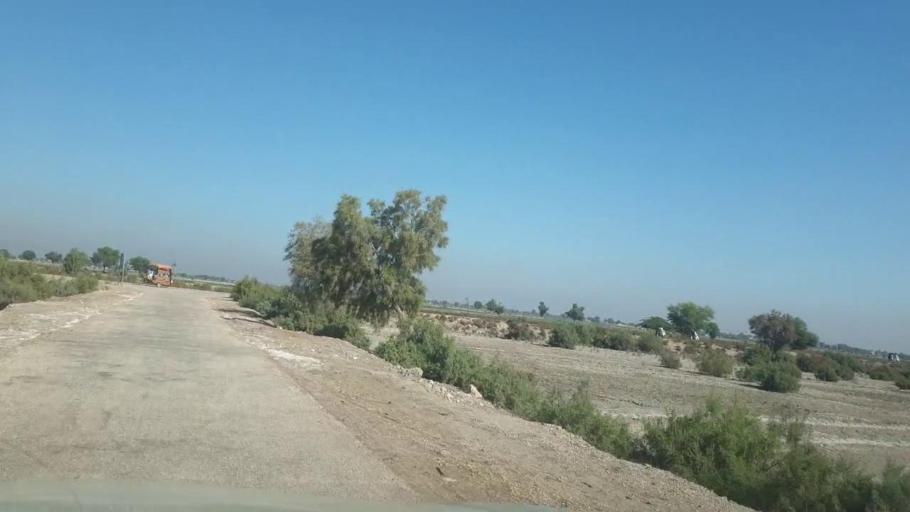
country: PK
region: Sindh
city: Bhan
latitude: 26.5409
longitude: 67.6442
